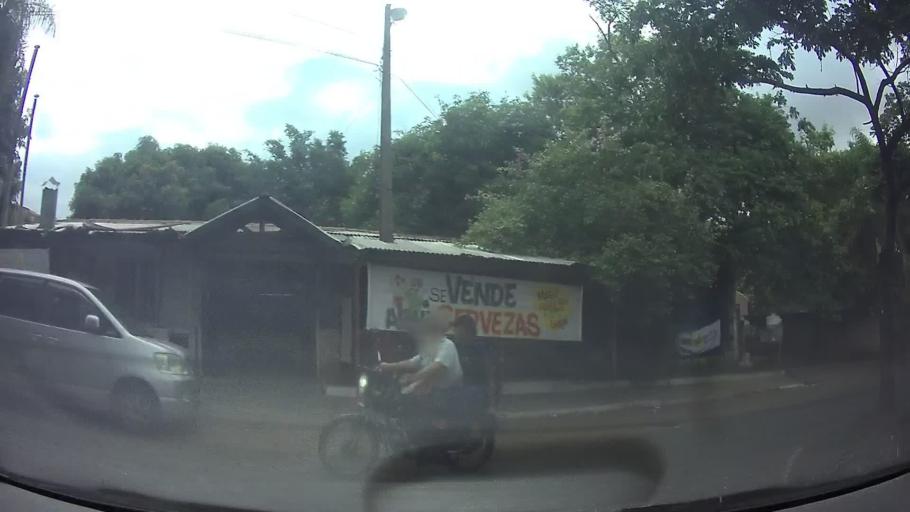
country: PY
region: Central
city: Fernando de la Mora
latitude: -25.3142
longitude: -57.5537
